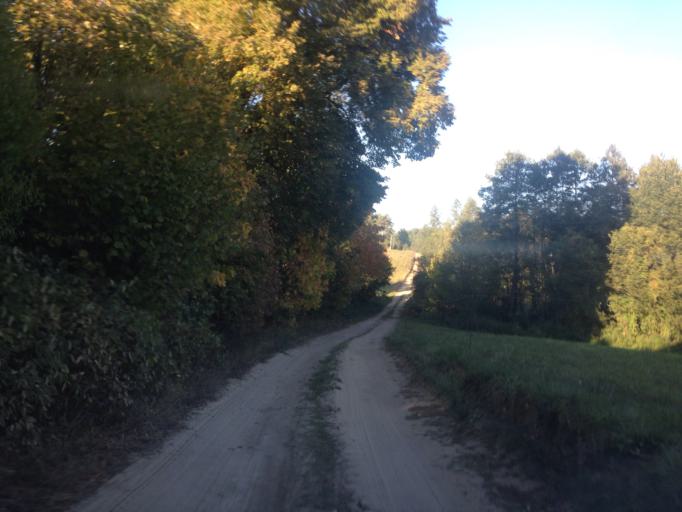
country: PL
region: Kujawsko-Pomorskie
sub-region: Powiat brodnicki
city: Bartniczka
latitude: 53.2686
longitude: 19.6710
